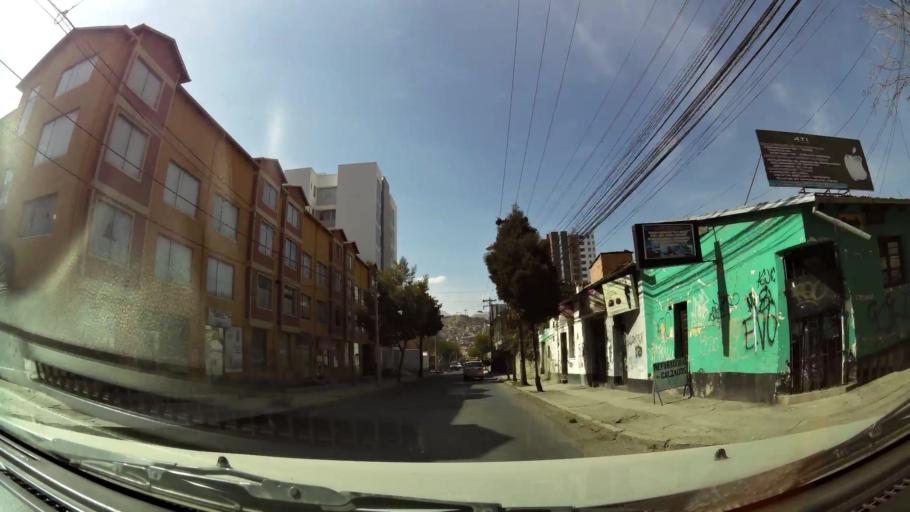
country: BO
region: La Paz
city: La Paz
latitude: -16.5275
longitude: -68.1043
